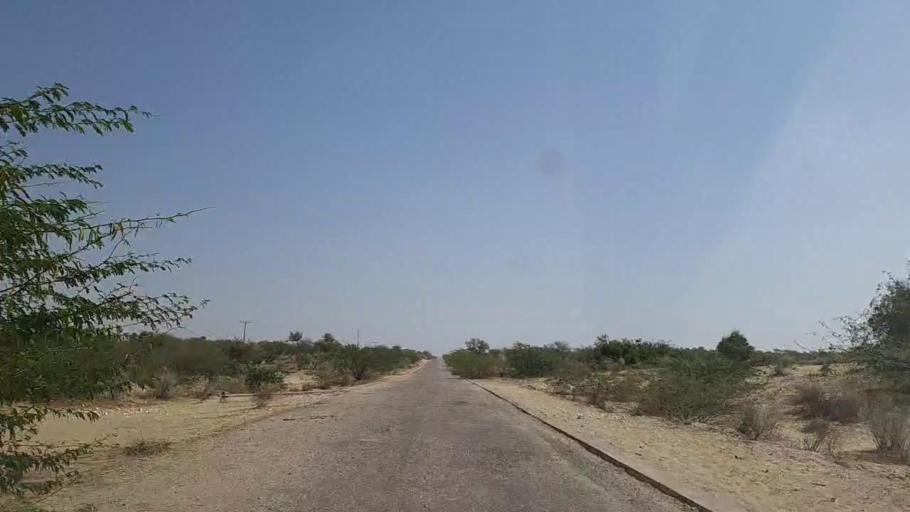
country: PK
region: Sindh
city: Diplo
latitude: 24.5144
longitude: 69.3826
